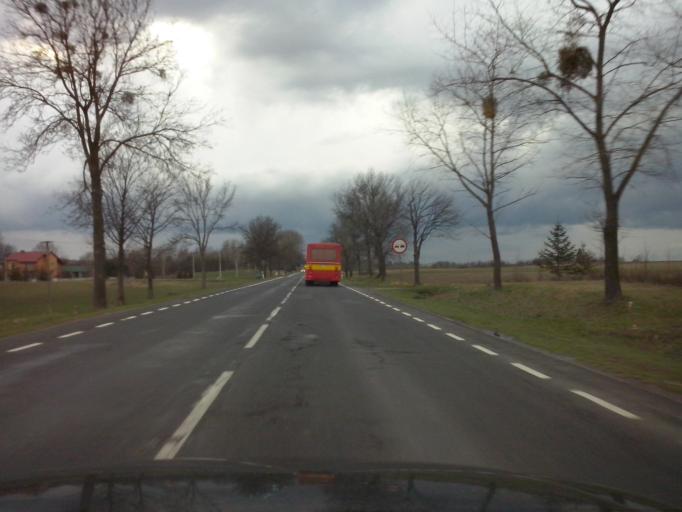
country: PL
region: Lublin Voivodeship
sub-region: Powiat chelmski
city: Rejowiec Fabryczny
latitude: 51.1723
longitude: 23.2919
